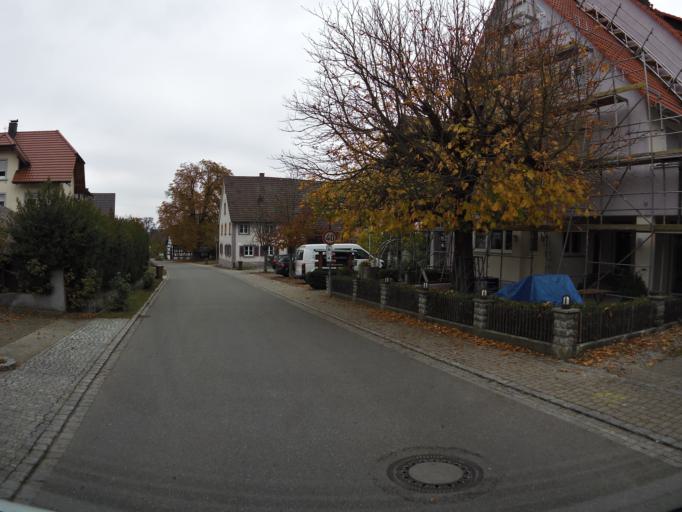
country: DE
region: Baden-Wuerttemberg
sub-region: Freiburg Region
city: Moos
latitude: 47.7085
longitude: 8.9301
